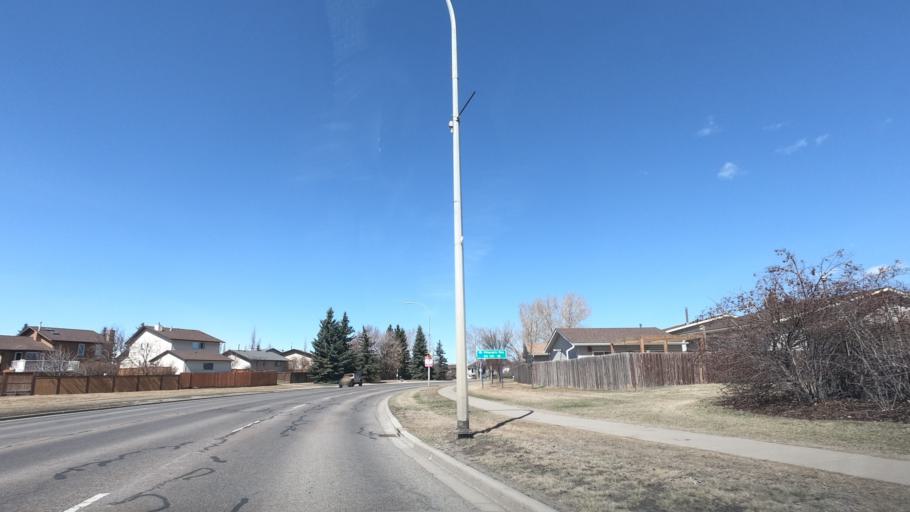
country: CA
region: Alberta
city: Airdrie
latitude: 51.2840
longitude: -114.0125
